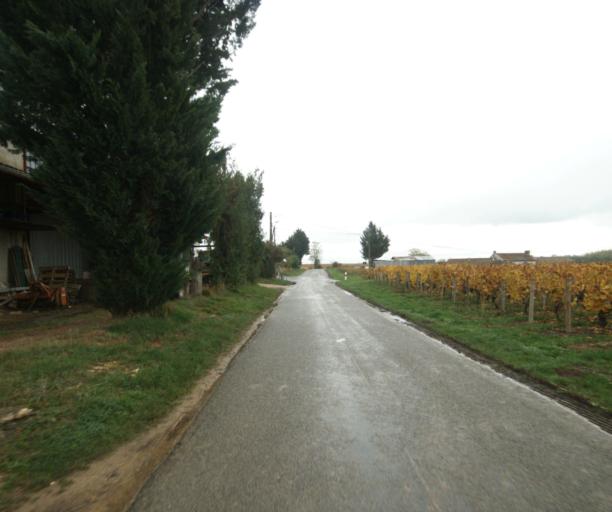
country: FR
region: Rhone-Alpes
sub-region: Departement de l'Ain
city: Pont-de-Vaux
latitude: 46.4779
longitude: 4.8610
